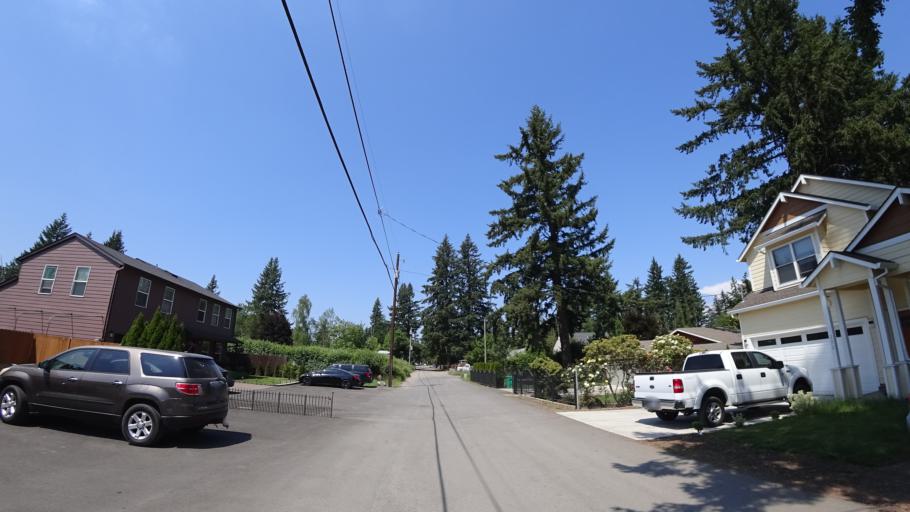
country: US
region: Oregon
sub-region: Multnomah County
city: Fairview
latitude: 45.5245
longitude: -122.5015
